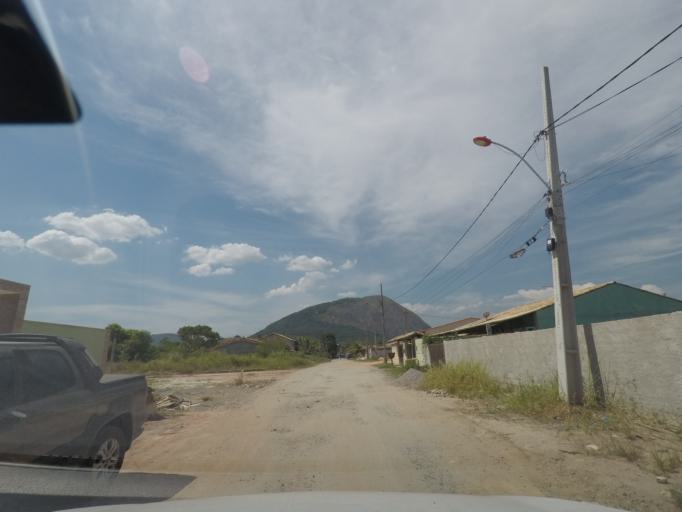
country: BR
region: Rio de Janeiro
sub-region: Marica
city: Marica
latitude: -22.9584
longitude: -42.9640
